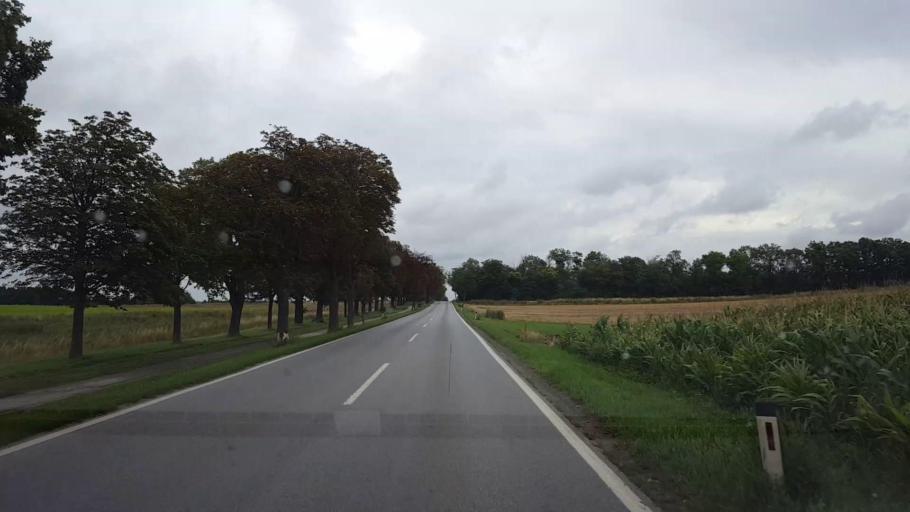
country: AT
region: Lower Austria
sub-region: Politischer Bezirk Wien-Umgebung
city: Rauchenwarth
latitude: 48.0840
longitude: 16.5153
